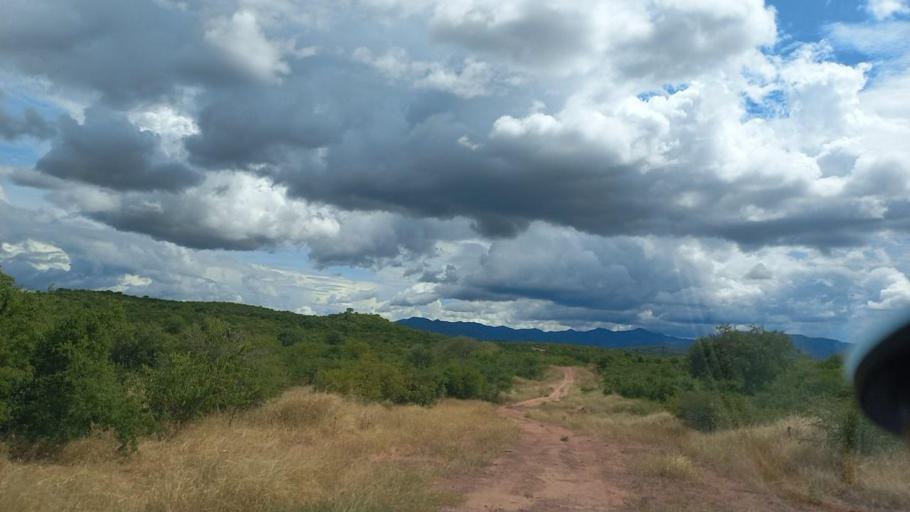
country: ZM
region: Lusaka
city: Luangwa
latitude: -15.6275
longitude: 30.3912
